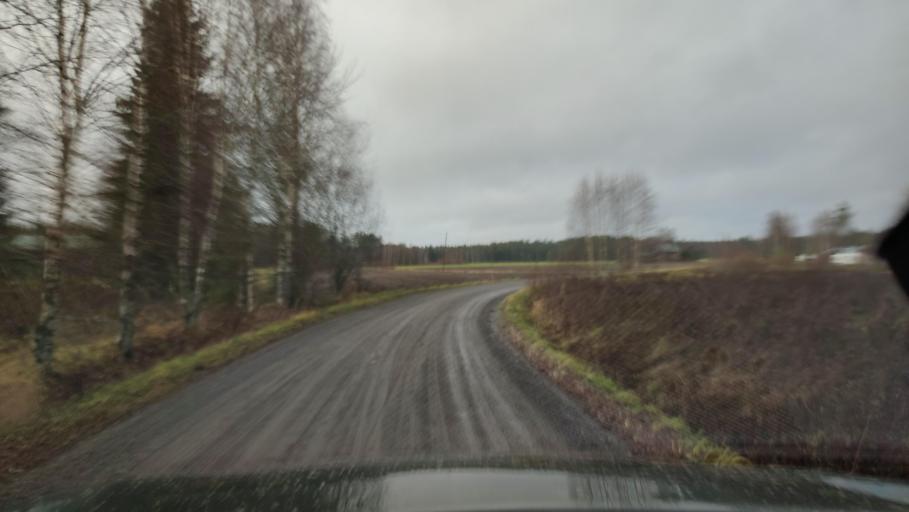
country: FI
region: Ostrobothnia
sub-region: Sydosterbotten
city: Naerpes
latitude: 62.4509
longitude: 21.5227
